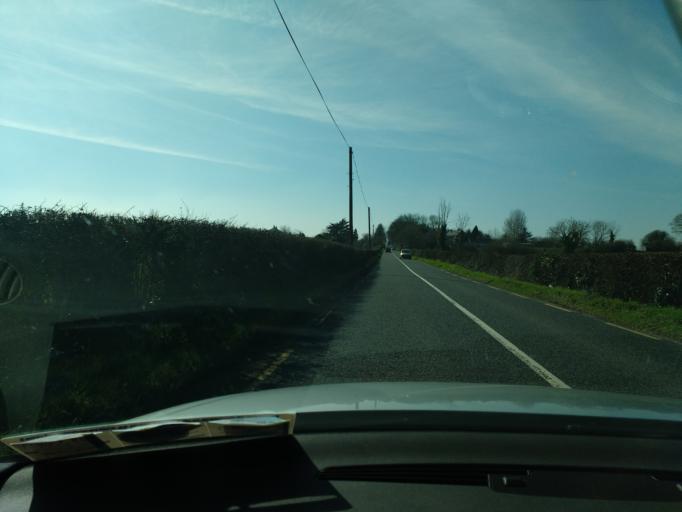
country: IE
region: Munster
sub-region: County Limerick
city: Castleconnell
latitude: 52.6958
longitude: -8.4655
